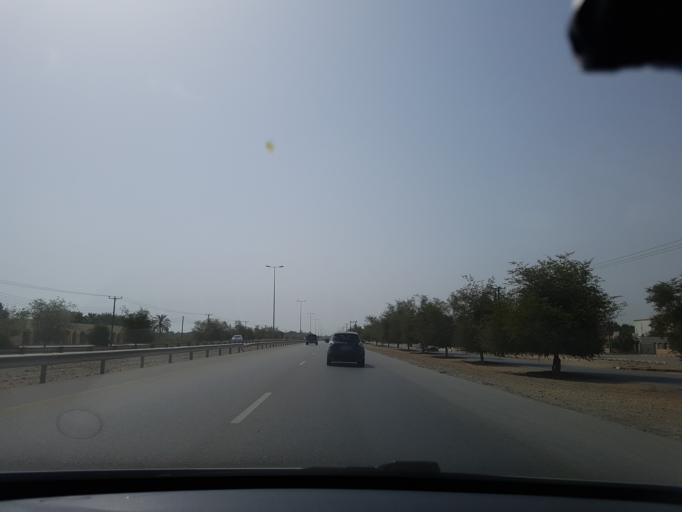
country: OM
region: Al Batinah
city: Al Khaburah
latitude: 23.9899
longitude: 57.0717
